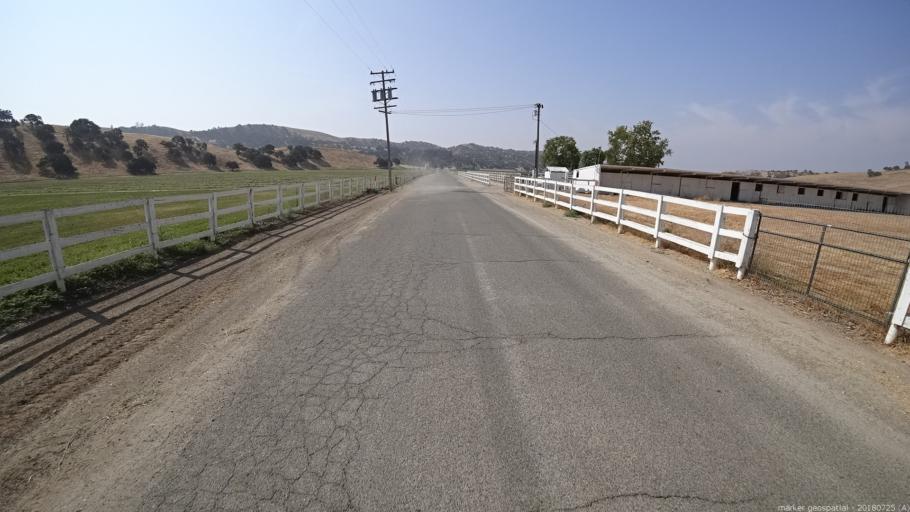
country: US
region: California
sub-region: San Luis Obispo County
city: San Miguel
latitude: 35.8302
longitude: -120.6551
